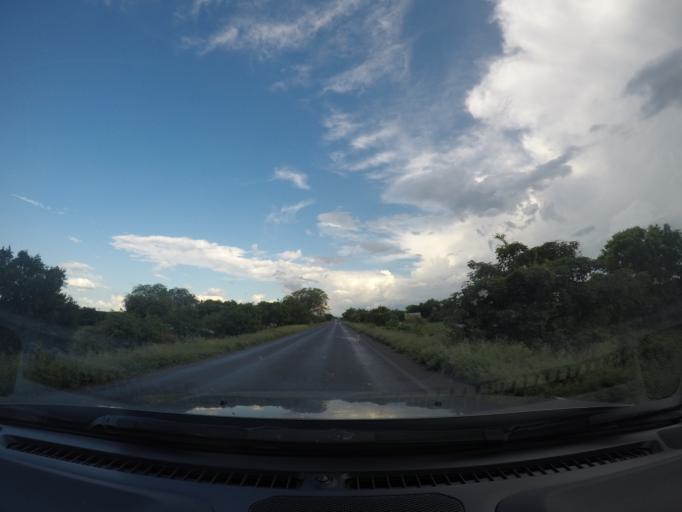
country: BR
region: Bahia
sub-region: Ibotirama
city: Ibotirama
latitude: -12.1402
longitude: -43.3224
